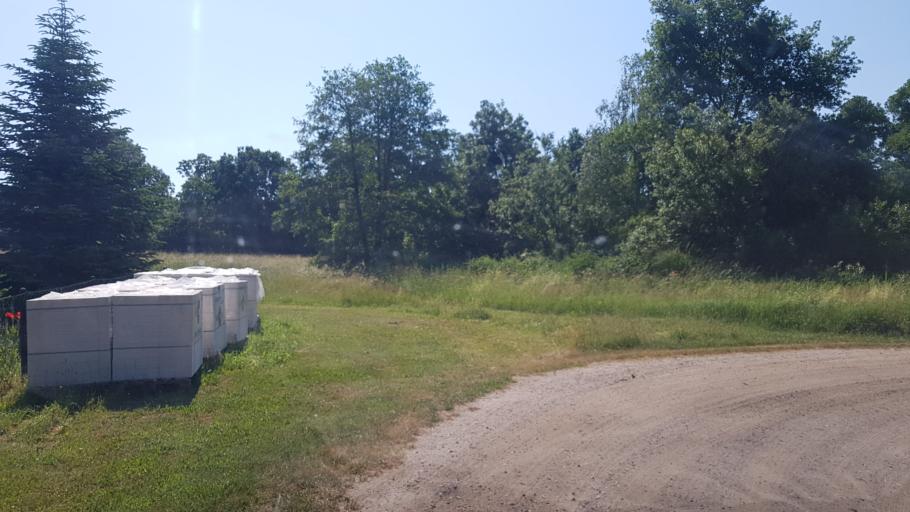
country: DE
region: Brandenburg
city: Lebusa
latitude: 51.7942
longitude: 13.4391
